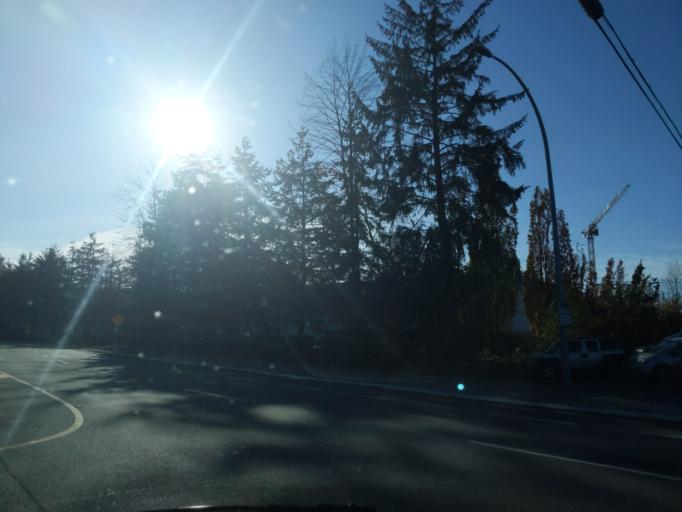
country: CA
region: British Columbia
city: New Westminster
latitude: 49.2047
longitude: -122.8673
